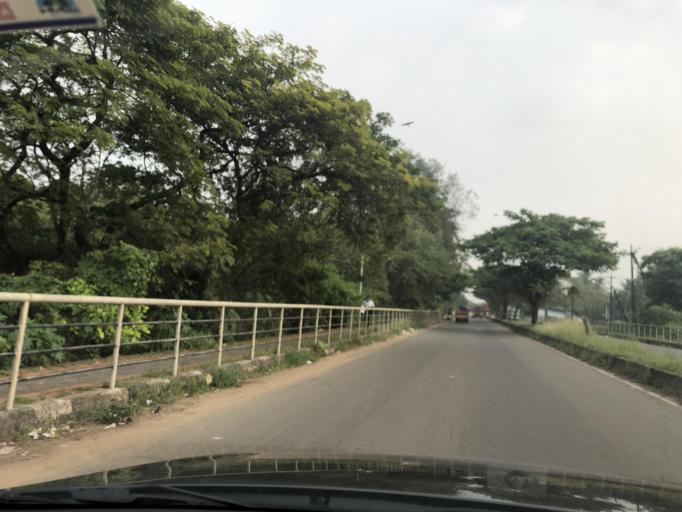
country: IN
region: Kerala
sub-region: Kozhikode
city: Kozhikode
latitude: 11.2859
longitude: 75.7603
